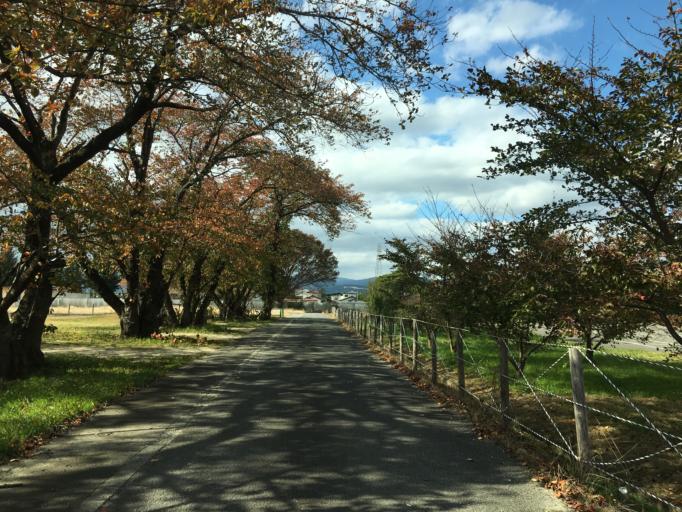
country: JP
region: Fukushima
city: Fukushima-shi
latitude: 37.8127
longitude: 140.4796
